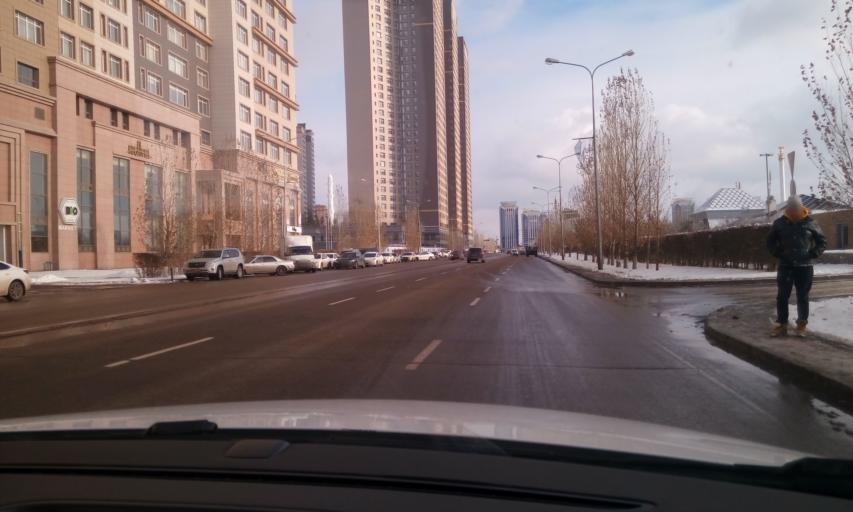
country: KZ
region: Astana Qalasy
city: Astana
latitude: 51.1266
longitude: 71.4620
